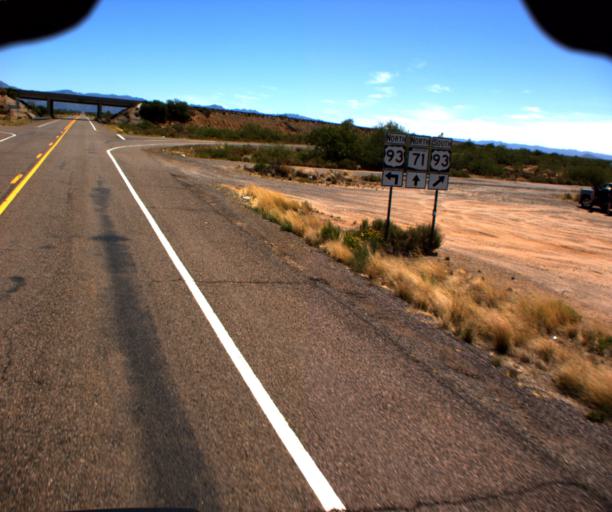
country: US
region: Arizona
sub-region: Yavapai County
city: Congress
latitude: 34.1227
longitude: -112.9523
